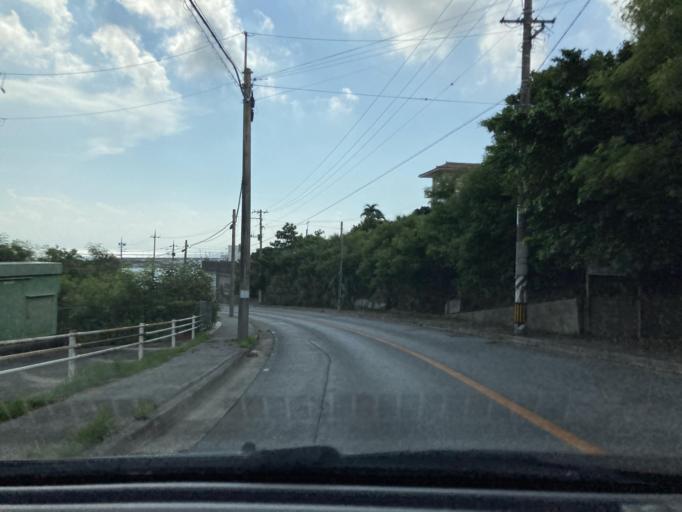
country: JP
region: Okinawa
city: Itoman
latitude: 26.1337
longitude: 127.7707
